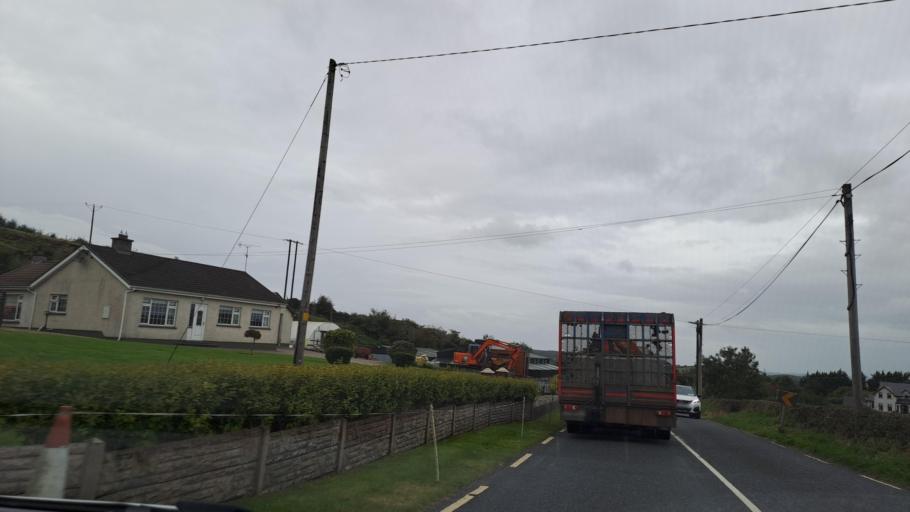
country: IE
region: Ulster
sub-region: County Monaghan
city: Castleblayney
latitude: 54.0902
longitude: -6.8353
